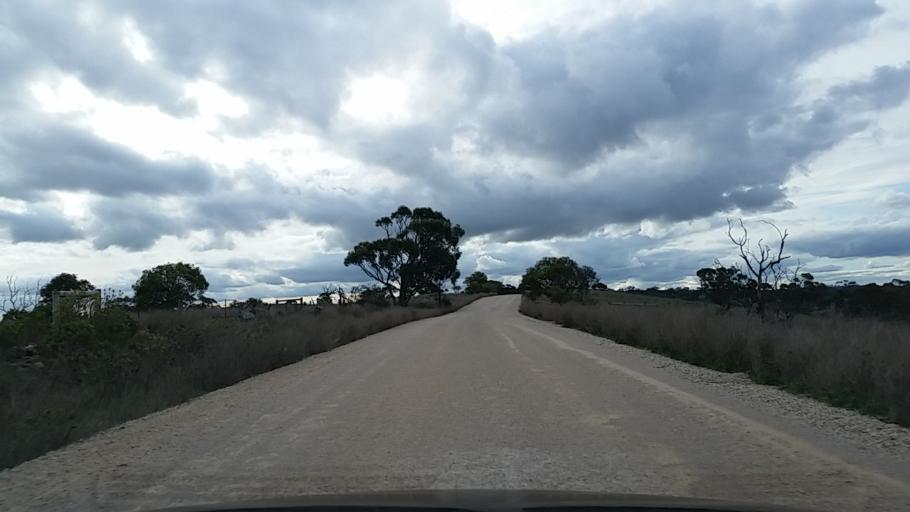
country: AU
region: South Australia
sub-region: Mount Barker
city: Callington
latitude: -35.0067
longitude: 139.0620
